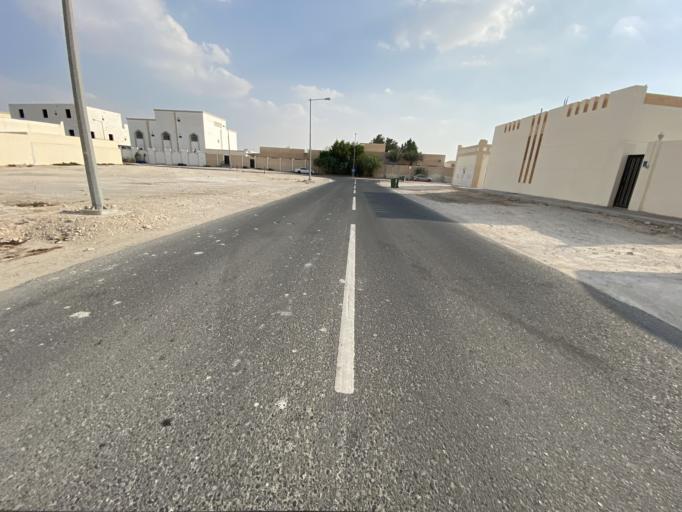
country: QA
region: Baladiyat ar Rayyan
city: Ar Rayyan
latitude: 25.2360
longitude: 51.3789
